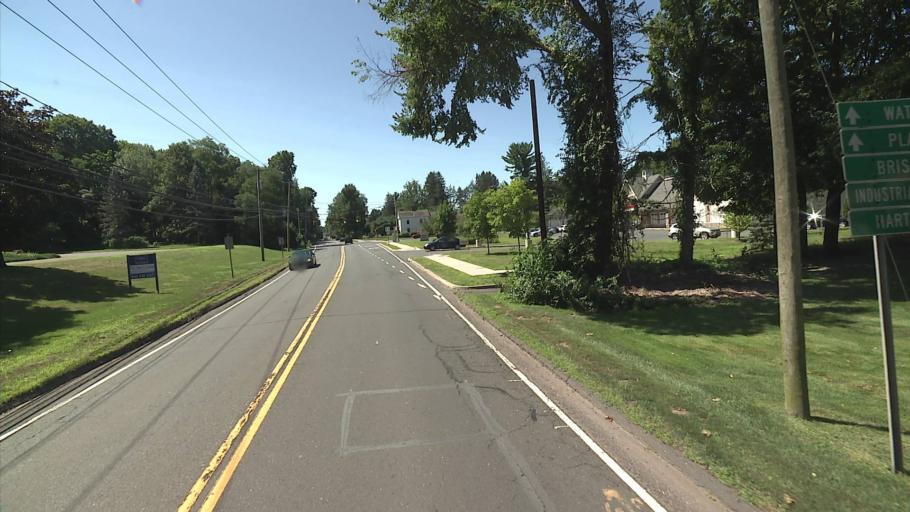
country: US
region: Connecticut
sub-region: Hartford County
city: Farmington
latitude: 41.7049
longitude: -72.8431
